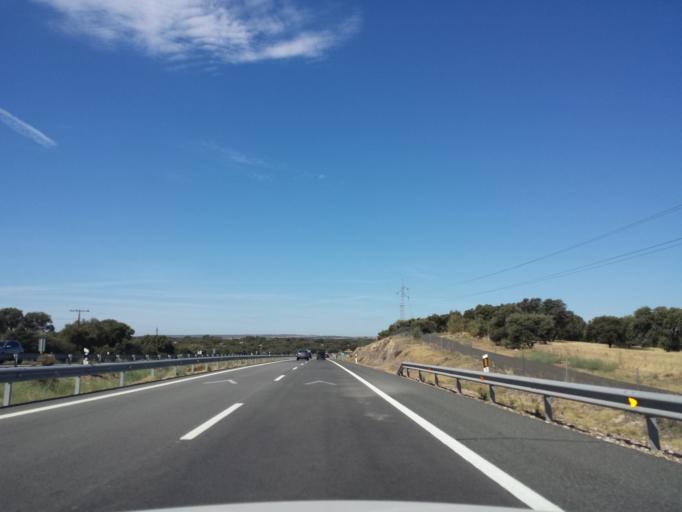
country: ES
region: Castille-La Mancha
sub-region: Province of Toledo
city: Alcanizo
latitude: 39.9174
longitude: -5.0650
